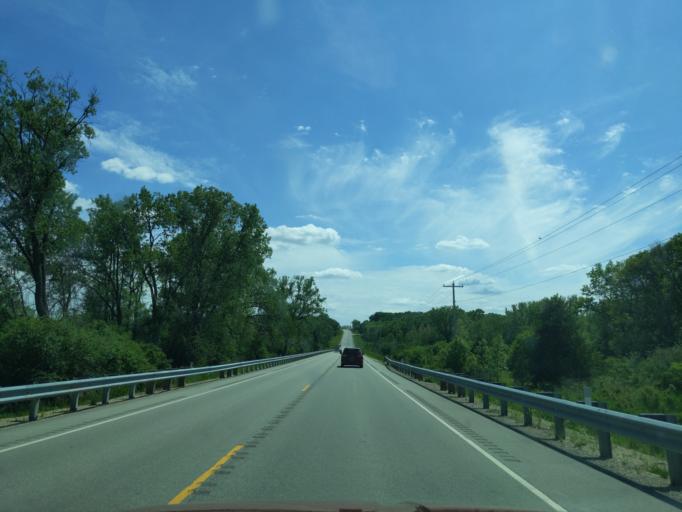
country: US
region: Wisconsin
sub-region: Columbia County
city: Rio
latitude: 43.4507
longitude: -89.3272
